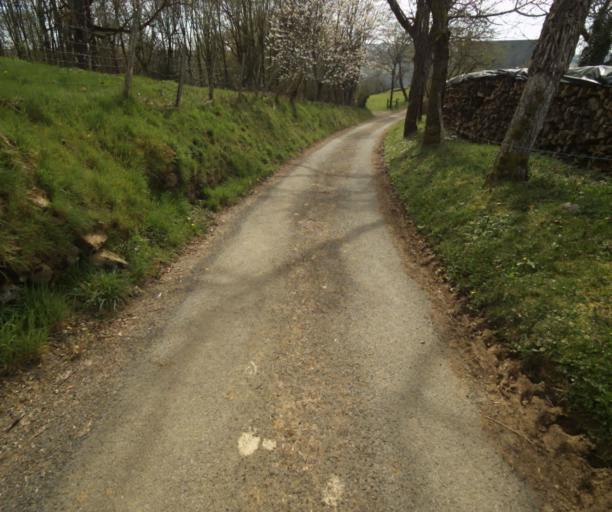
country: FR
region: Limousin
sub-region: Departement de la Correze
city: Correze
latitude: 45.3584
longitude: 1.8163
